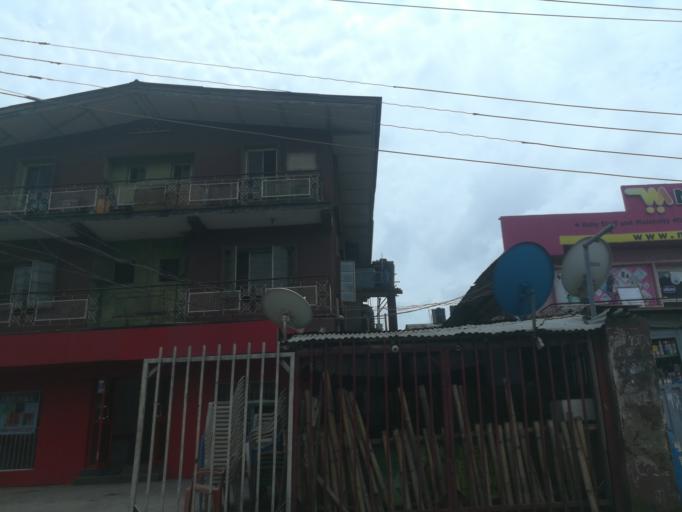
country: NG
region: Lagos
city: Somolu
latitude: 6.5296
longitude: 3.3874
